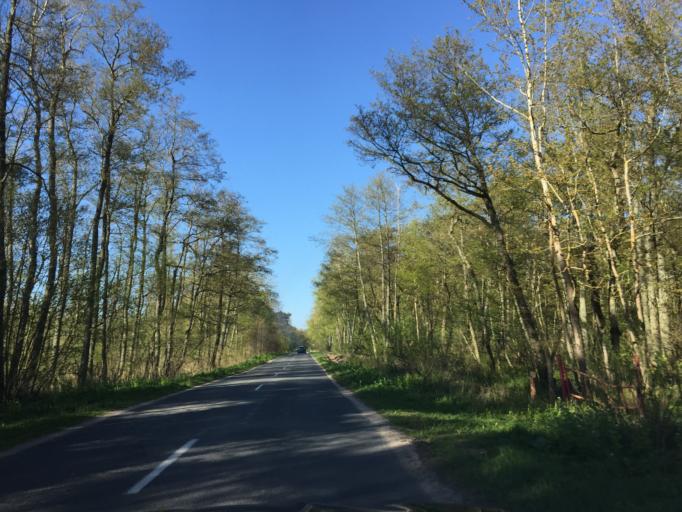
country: LT
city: Nida
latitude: 55.2106
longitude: 20.8788
